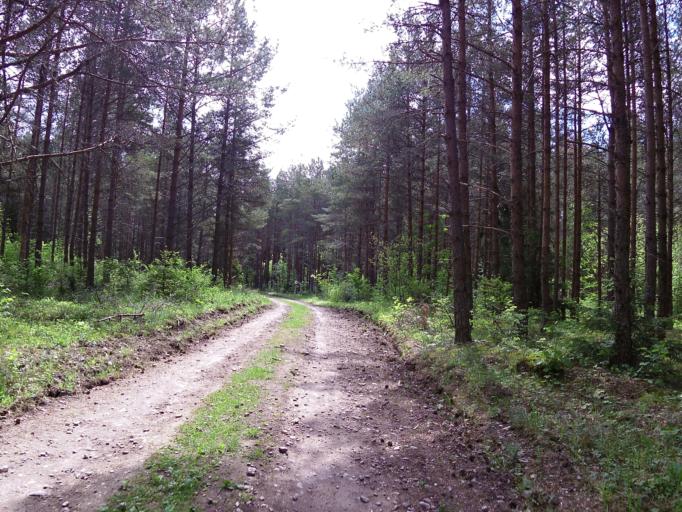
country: EE
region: Harju
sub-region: Paldiski linn
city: Paldiski
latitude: 59.2605
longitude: 23.7454
